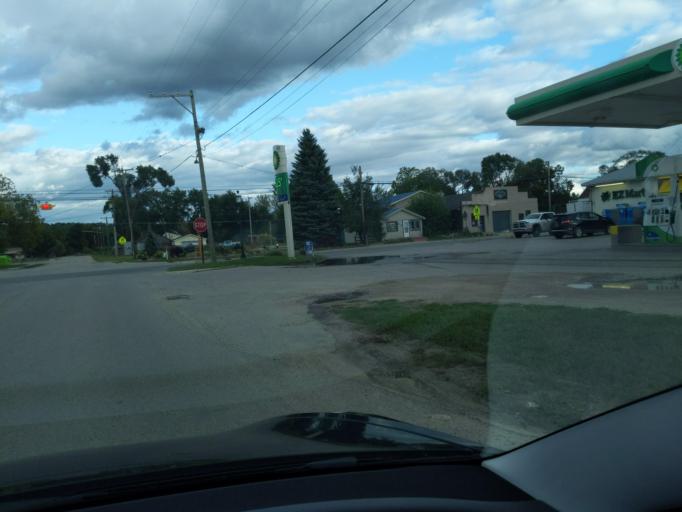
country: US
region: Michigan
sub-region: Kalkaska County
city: Rapid City
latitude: 44.8343
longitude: -85.2833
